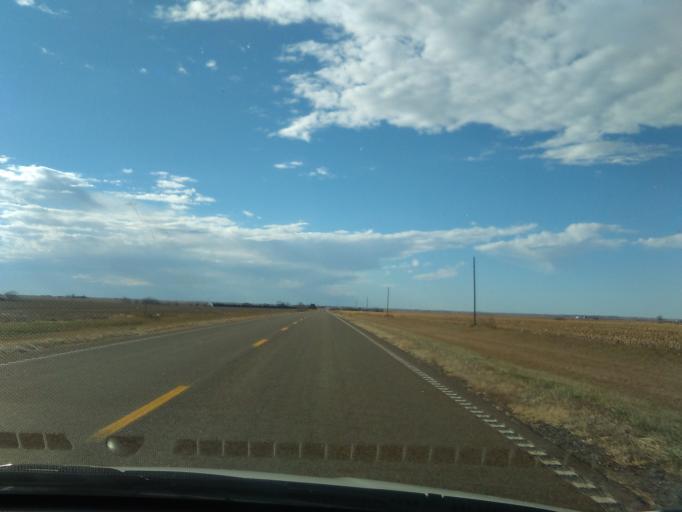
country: US
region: Nebraska
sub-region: Webster County
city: Red Cloud
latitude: 40.2921
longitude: -98.5597
